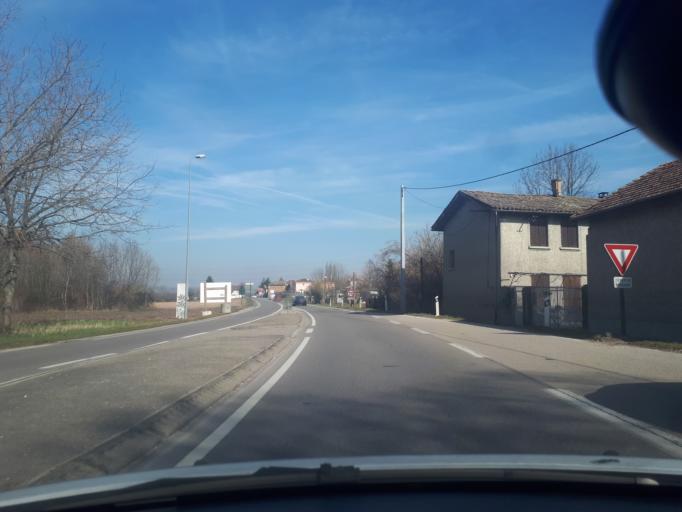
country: FR
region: Rhone-Alpes
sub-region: Departement de l'Isere
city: Saint-Savin
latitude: 45.6340
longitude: 5.2956
